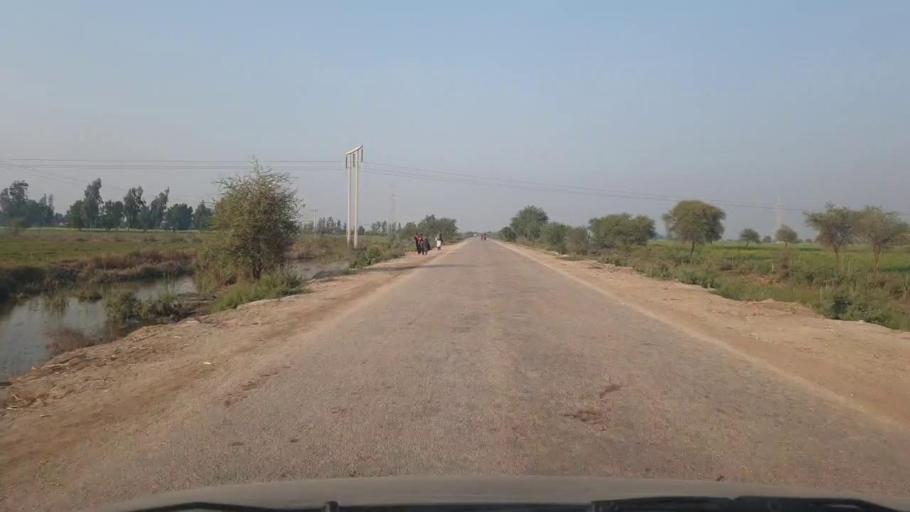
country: PK
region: Sindh
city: Mirwah Gorchani
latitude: 25.3153
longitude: 69.1644
